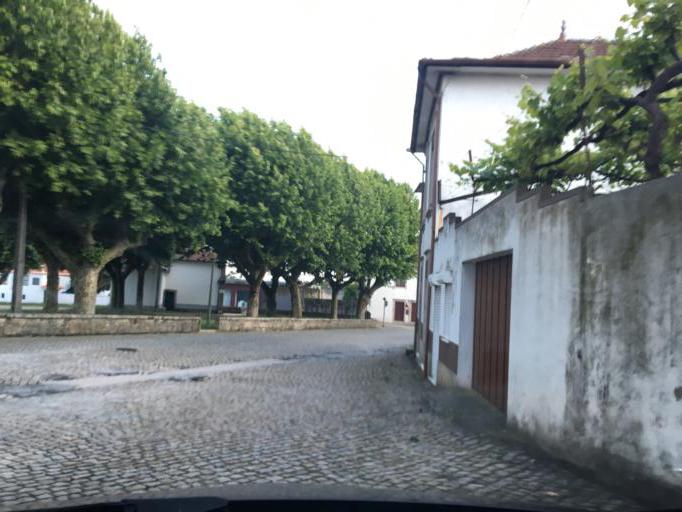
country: PT
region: Porto
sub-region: Maia
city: Anta
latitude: 41.2479
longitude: -8.6363
